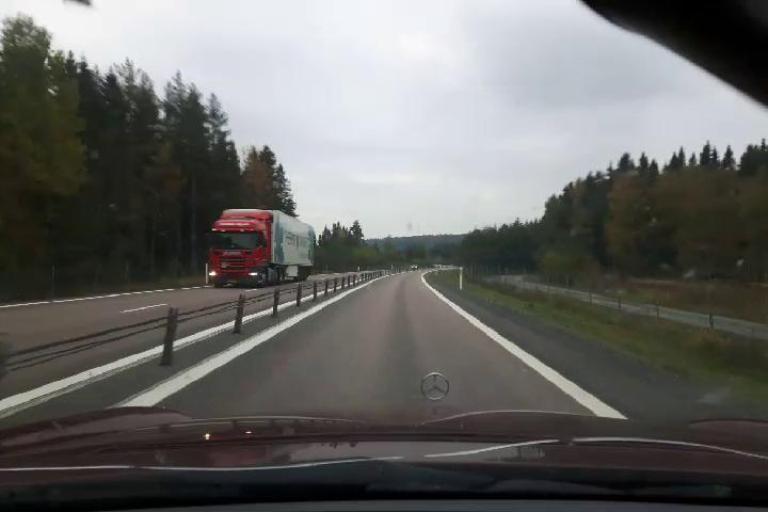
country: SE
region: Vaesternorrland
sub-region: Kramfors Kommun
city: Nordingra
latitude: 62.9136
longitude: 18.0937
